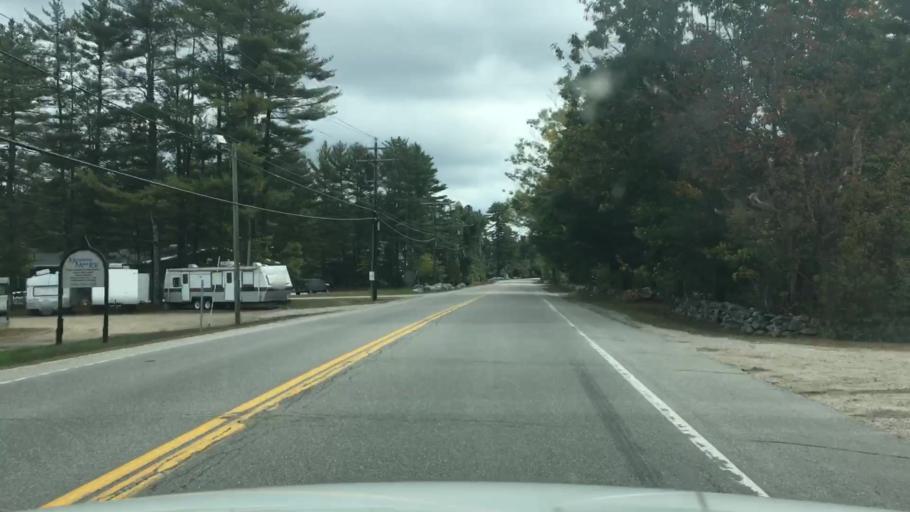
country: US
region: New Hampshire
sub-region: Carroll County
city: Tamworth
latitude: 43.8741
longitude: -71.2175
